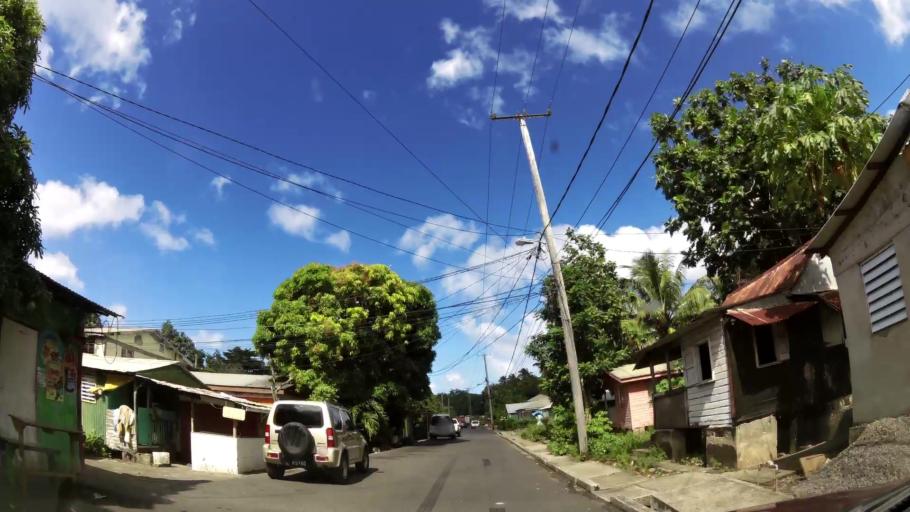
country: DM
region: Saint John
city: Portsmouth
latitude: 15.5822
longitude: -61.4604
